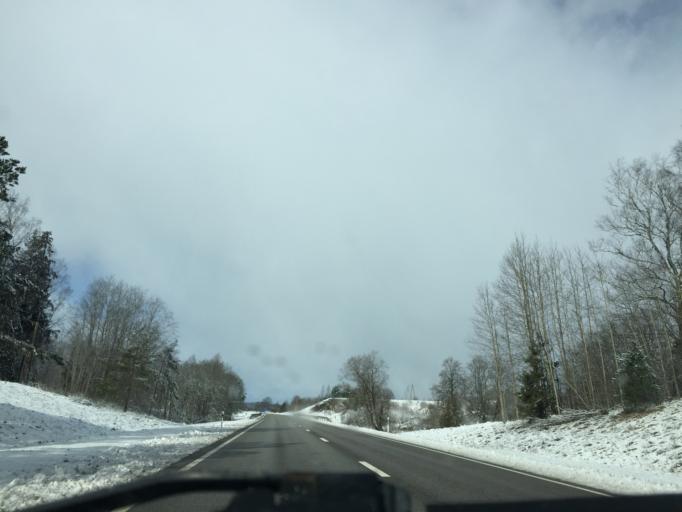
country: LV
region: Talsu Rajons
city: Talsi
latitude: 57.1636
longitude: 22.6719
